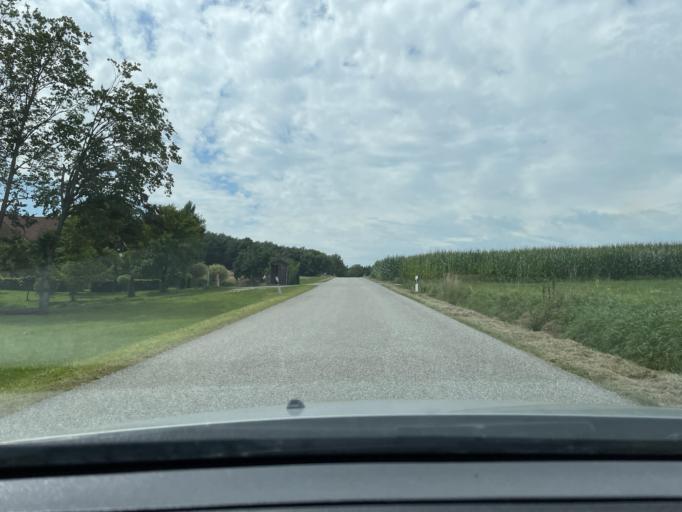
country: DE
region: Bavaria
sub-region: Lower Bavaria
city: Geisenhausen
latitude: 48.4431
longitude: 12.2432
